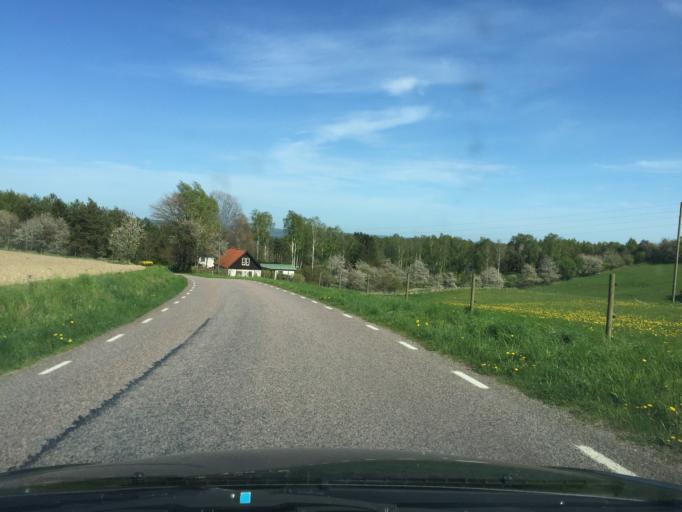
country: SE
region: Skane
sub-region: Sjobo Kommun
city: Blentarp
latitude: 55.5694
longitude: 13.5603
